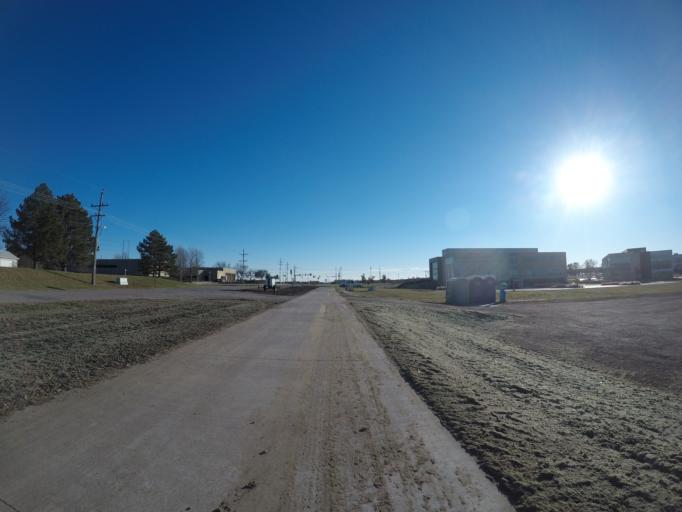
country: US
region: Kansas
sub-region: Riley County
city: Manhattan
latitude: 39.2061
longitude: -96.5857
